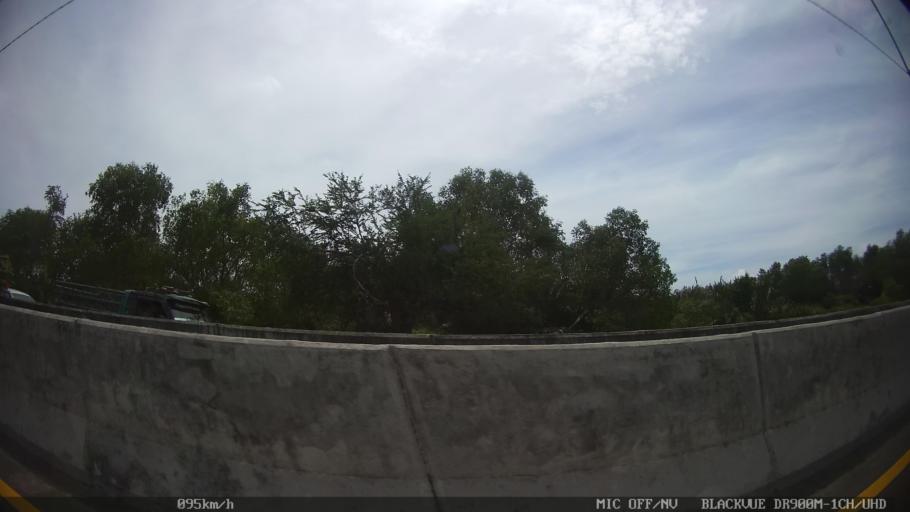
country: ID
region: North Sumatra
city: Belawan
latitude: 3.7526
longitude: 98.6821
